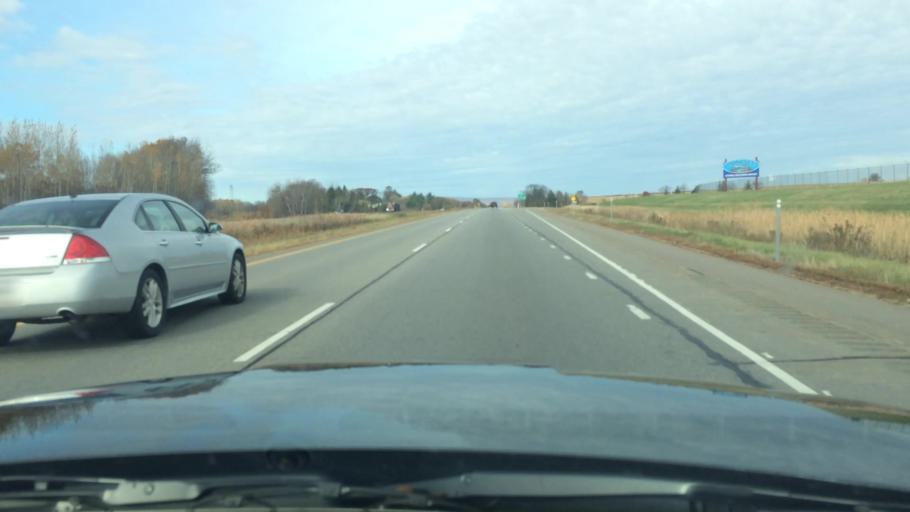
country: US
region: Wisconsin
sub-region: Marathon County
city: Mosinee
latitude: 44.7817
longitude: -89.6801
